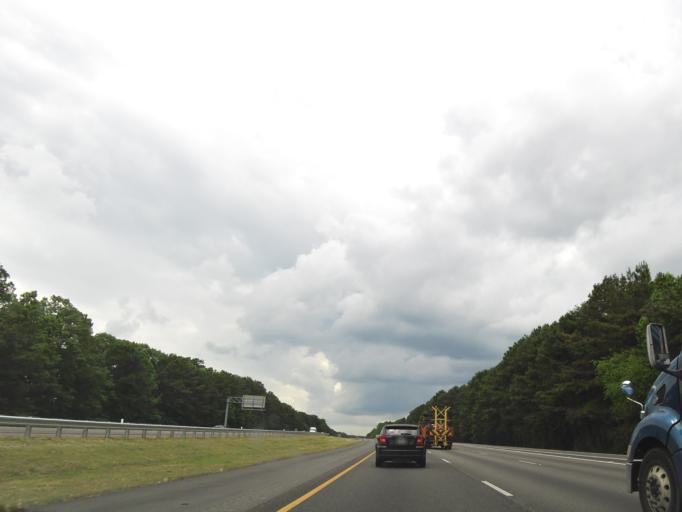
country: US
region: Georgia
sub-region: Douglas County
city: Douglasville
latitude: 33.7275
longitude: -84.7653
